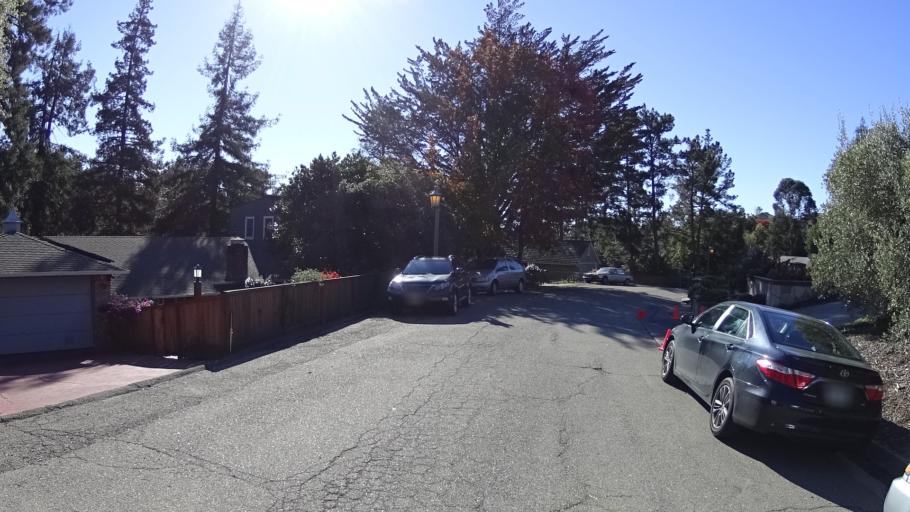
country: US
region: California
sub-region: Alameda County
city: Piedmont
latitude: 37.8437
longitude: -122.2351
